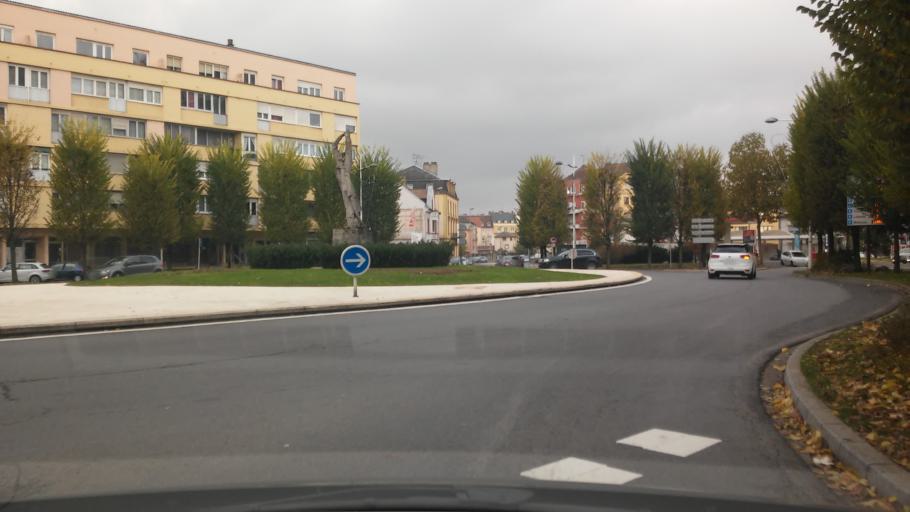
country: FR
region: Lorraine
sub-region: Departement de la Moselle
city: Thionville
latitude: 49.3515
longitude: 6.1601
